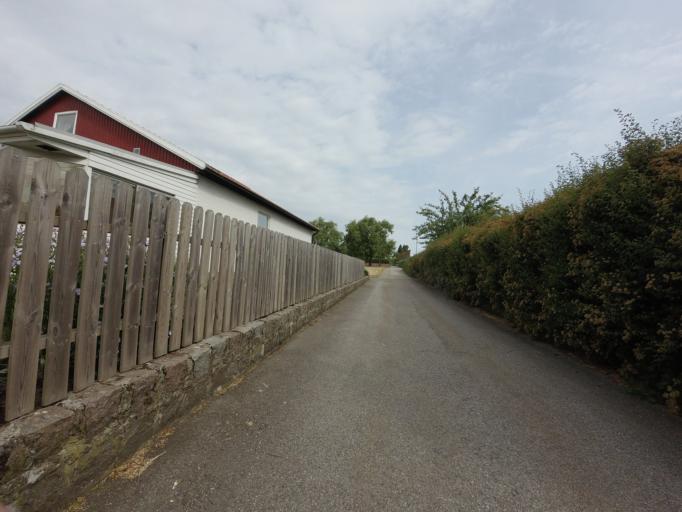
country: SE
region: Skane
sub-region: Staffanstorps Kommun
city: Hjaerup
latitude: 55.6611
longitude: 13.1106
